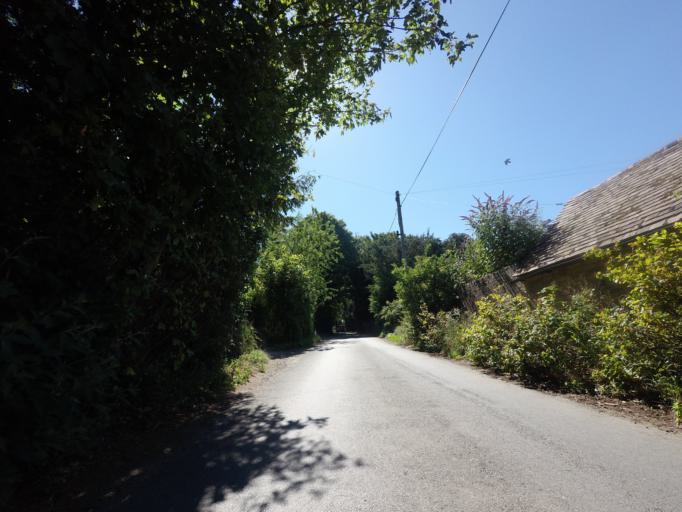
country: GB
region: England
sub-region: Kent
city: Ash
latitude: 51.2978
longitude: 1.2368
